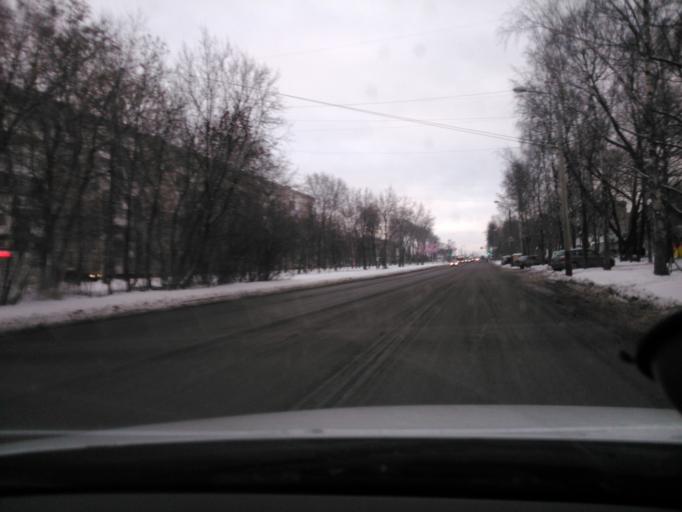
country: RU
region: Perm
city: Kondratovo
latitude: 57.9651
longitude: 56.1769
